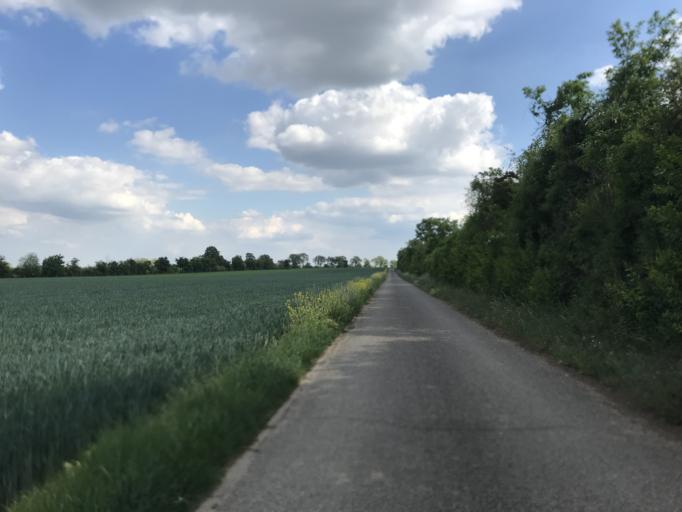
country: DE
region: Rheinland-Pfalz
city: Nieder-Ingelheim
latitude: 49.9733
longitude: 8.0942
